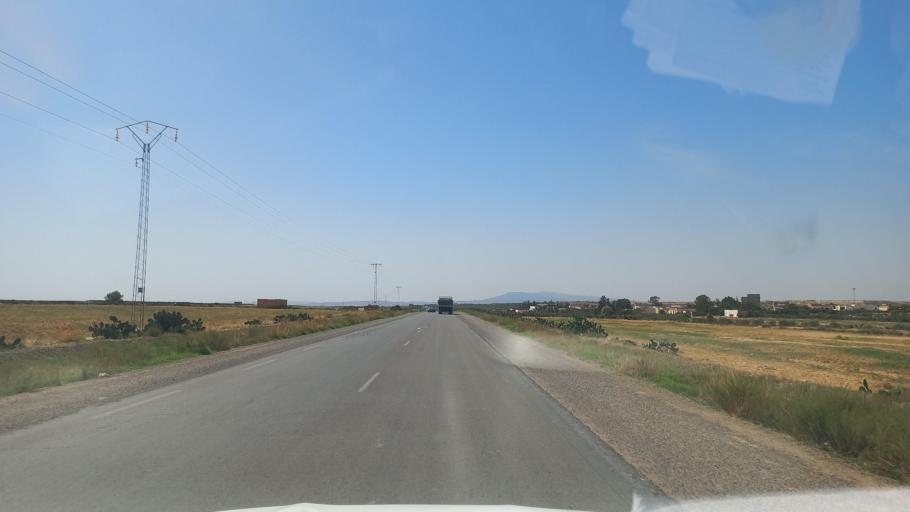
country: TN
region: Al Qasrayn
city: Sbiba
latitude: 35.3664
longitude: 9.0959
